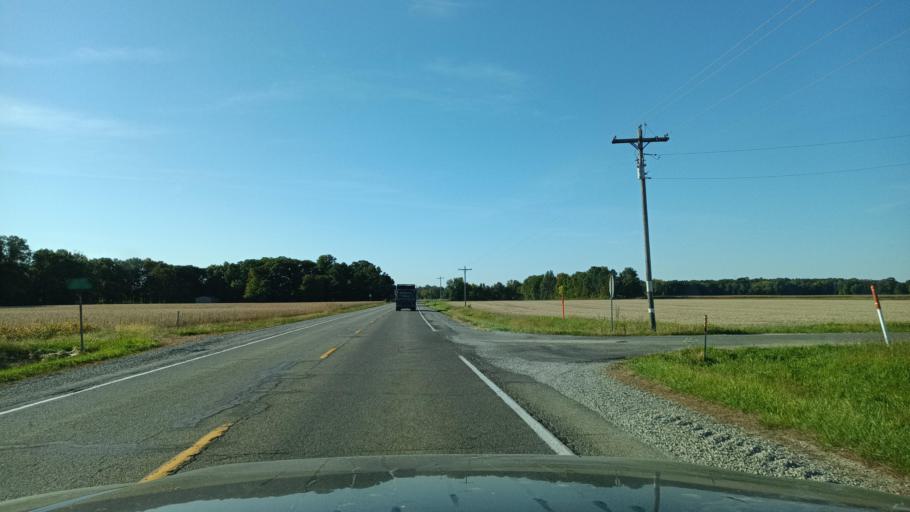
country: US
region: Illinois
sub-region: Clark County
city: Marshall
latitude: 39.4519
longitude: -87.6821
